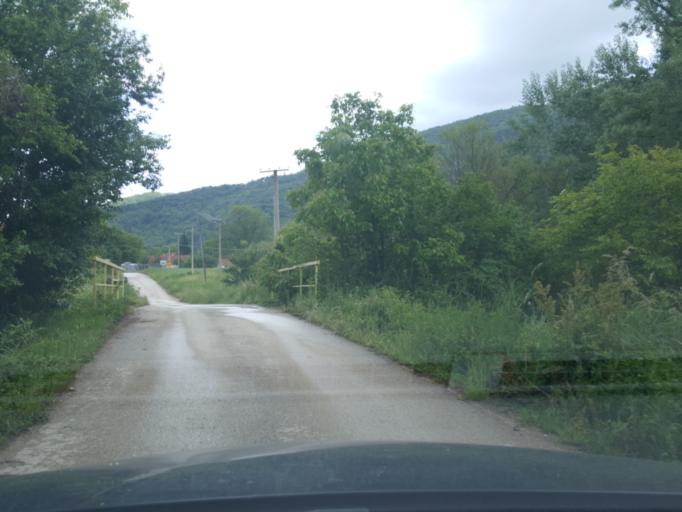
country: RS
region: Central Serbia
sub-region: Zajecarski Okrug
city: Soko Banja
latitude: 43.6350
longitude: 21.9871
